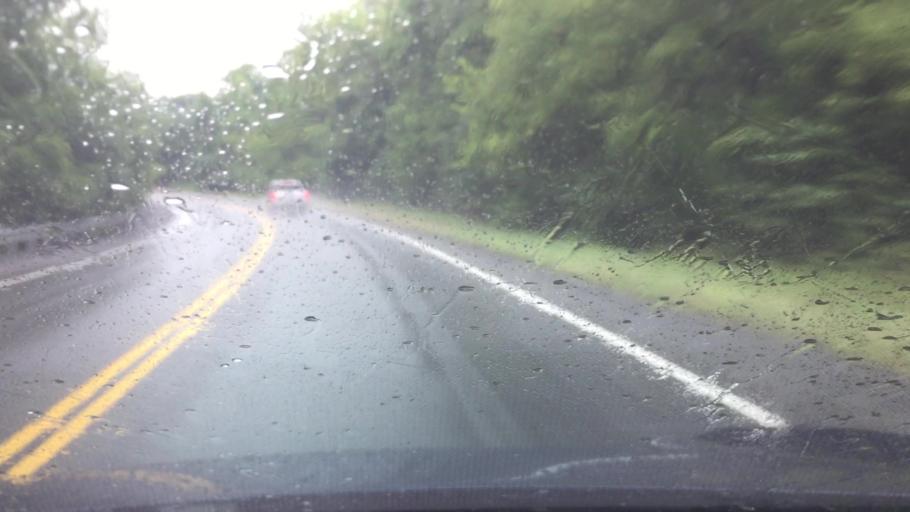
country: US
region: Virginia
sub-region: City of Bedford
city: Bedford
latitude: 37.3549
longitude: -79.4738
